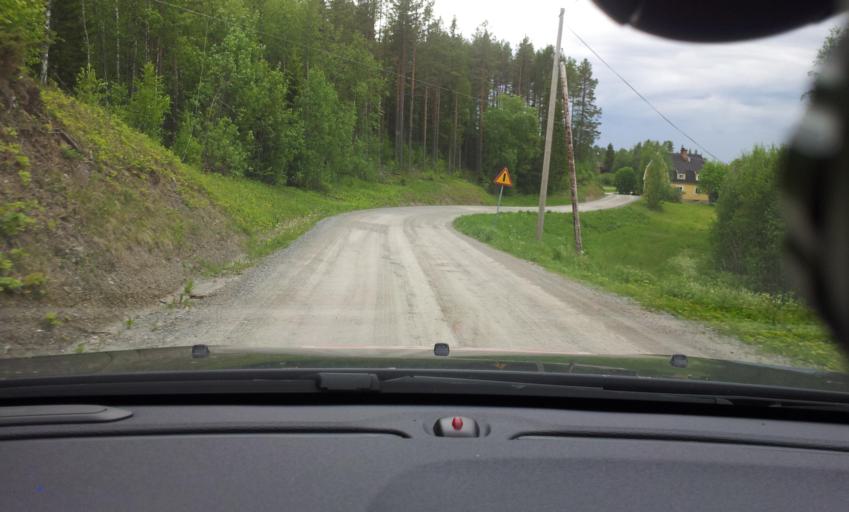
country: SE
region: Jaemtland
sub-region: OEstersunds Kommun
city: Brunflo
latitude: 62.9802
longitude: 14.6956
